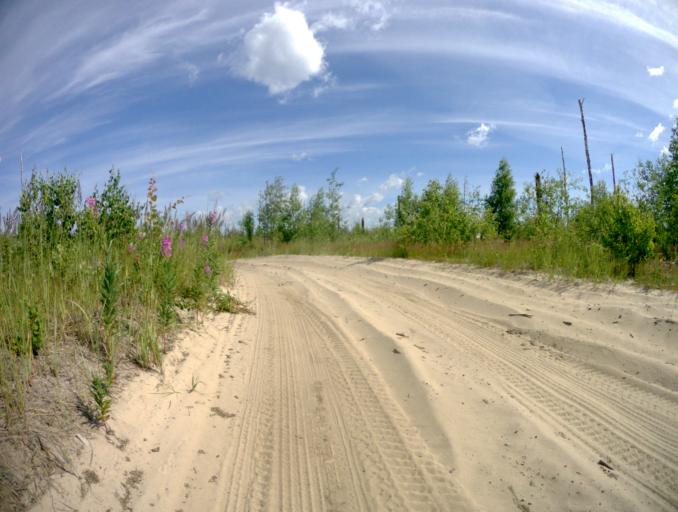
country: RU
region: Ivanovo
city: Talitsy
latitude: 56.5154
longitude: 42.3982
